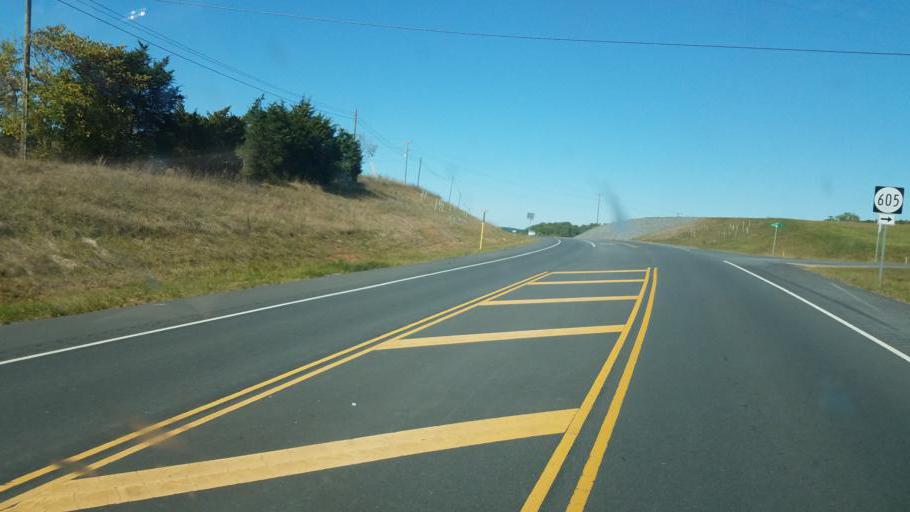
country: US
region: Virginia
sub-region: Warren County
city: Front Royal
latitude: 38.8729
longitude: -78.2470
